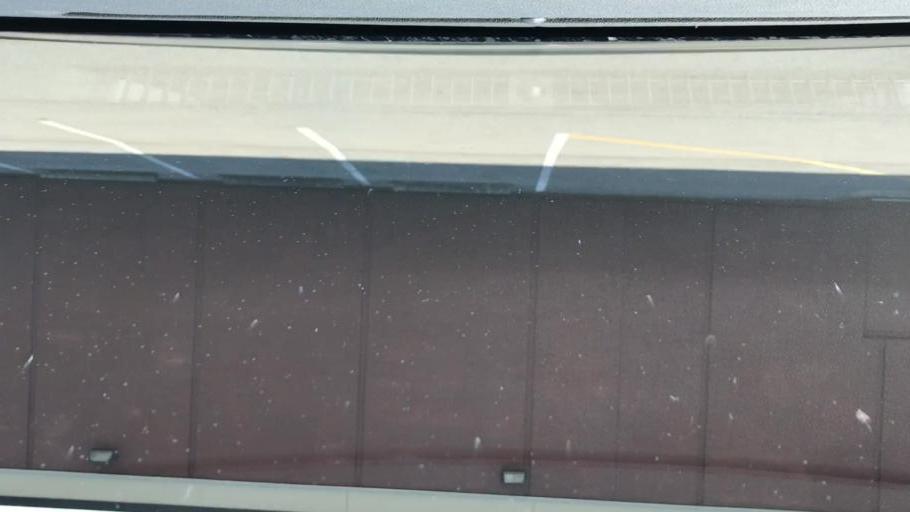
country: US
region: Tennessee
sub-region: Williamson County
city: Brentwood
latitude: 36.0282
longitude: -86.7902
